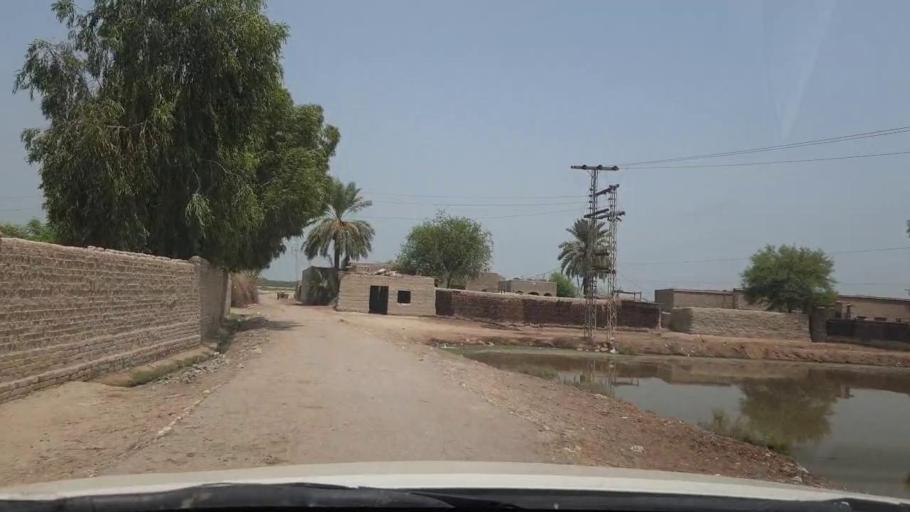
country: PK
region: Sindh
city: Rustam jo Goth
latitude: 28.0169
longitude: 68.7838
